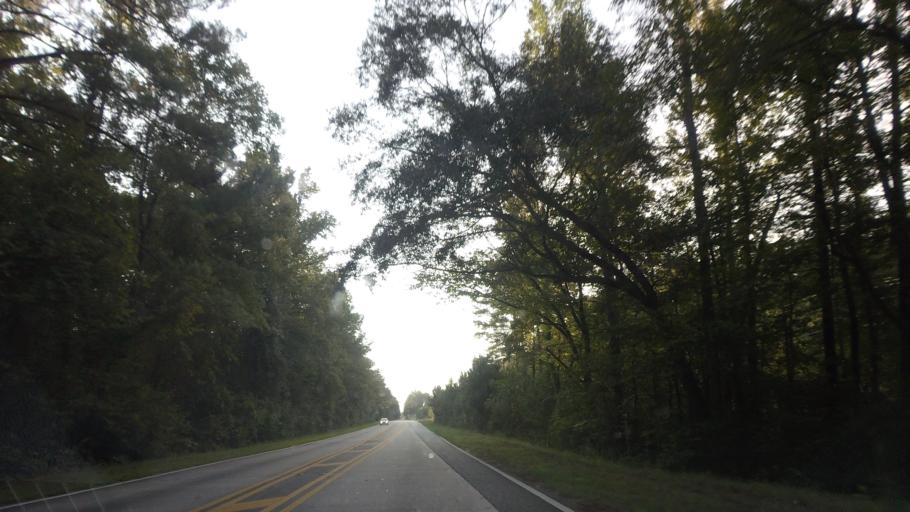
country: US
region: Georgia
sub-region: Bibb County
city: Macon
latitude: 32.9383
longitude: -83.7343
